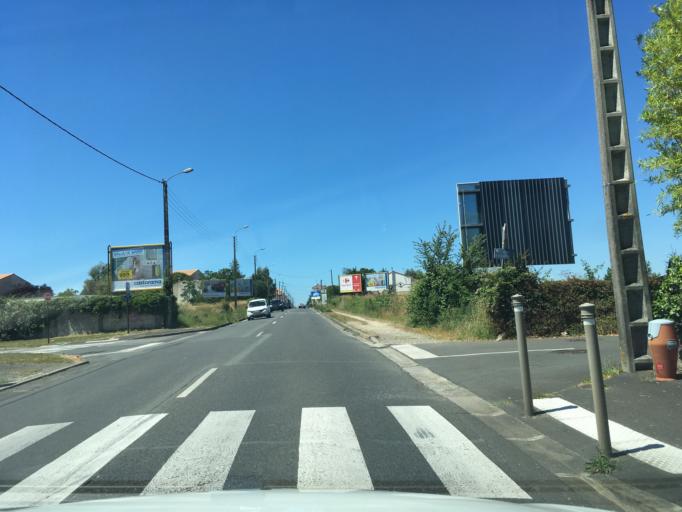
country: FR
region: Poitou-Charentes
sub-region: Departement des Deux-Sevres
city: Aiffres
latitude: 46.3171
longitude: -0.4283
